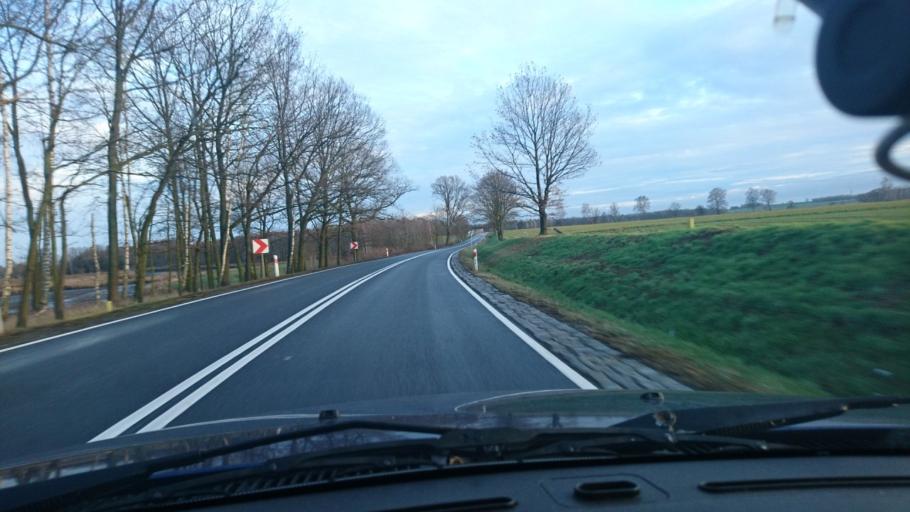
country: PL
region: Lodz Voivodeship
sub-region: Powiat wieruszowski
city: Boleslawiec
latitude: 51.1559
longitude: 18.1735
